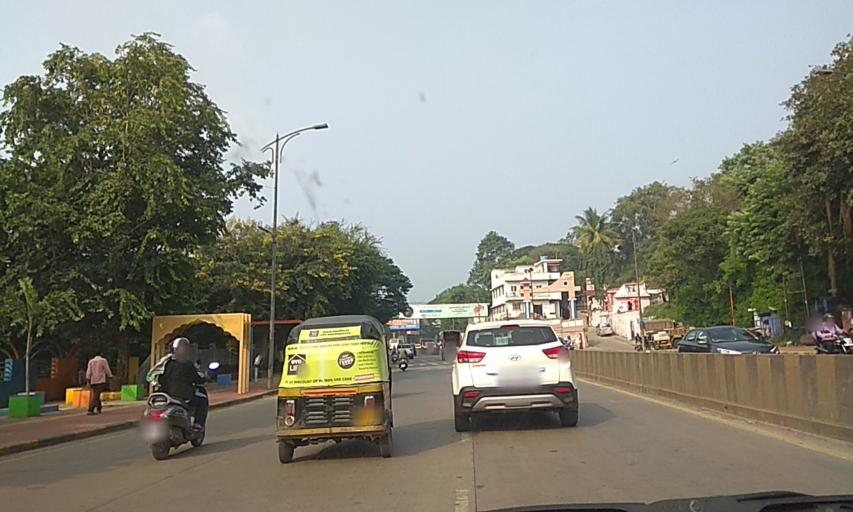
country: IN
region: Maharashtra
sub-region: Pune Division
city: Shivaji Nagar
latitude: 18.5441
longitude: 73.8808
